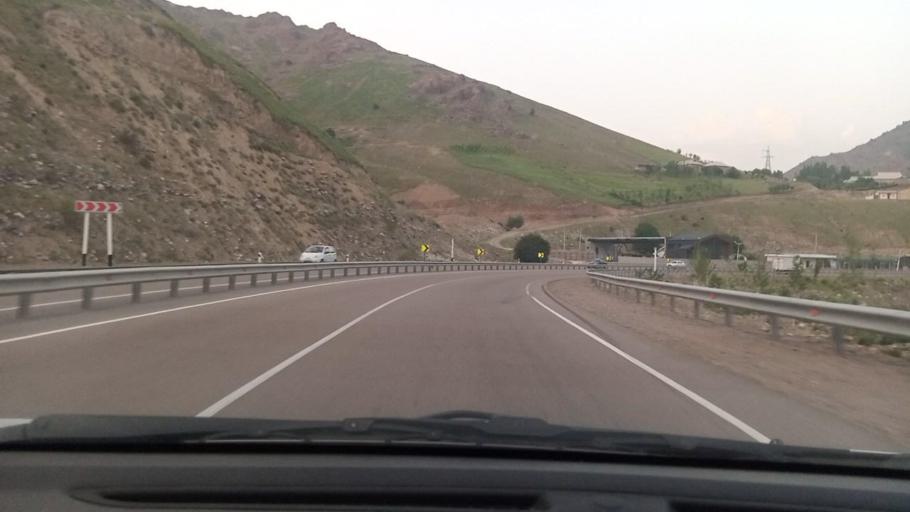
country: UZ
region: Toshkent
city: Angren
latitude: 41.1260
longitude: 70.3571
